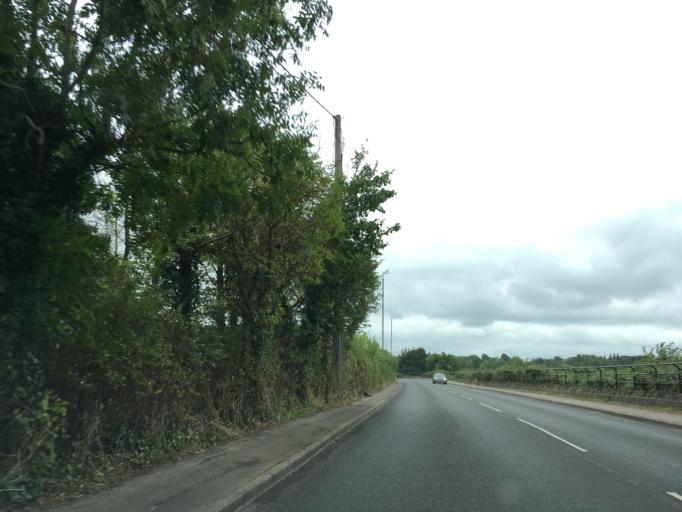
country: GB
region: England
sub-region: Bath and North East Somerset
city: Keynsham
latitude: 51.4236
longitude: -2.4872
